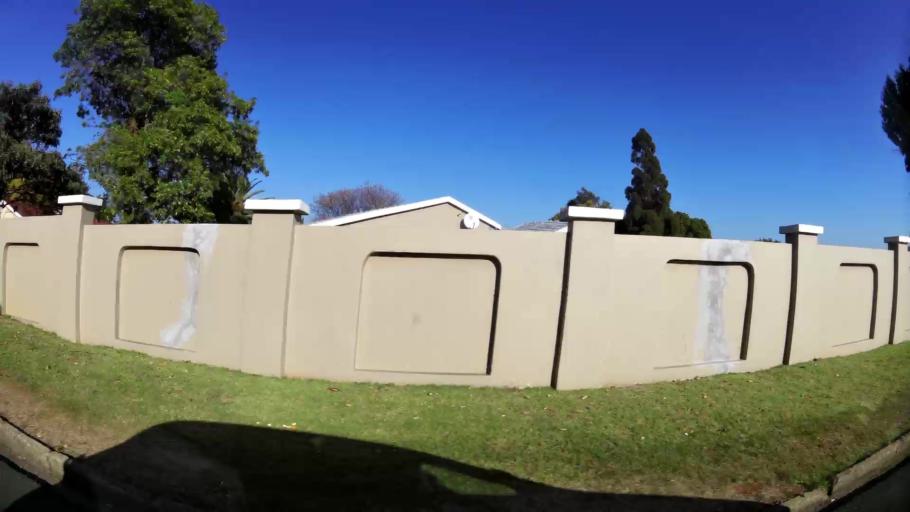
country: ZA
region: Gauteng
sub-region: City of Johannesburg Metropolitan Municipality
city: Modderfontein
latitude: -26.1407
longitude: 28.1656
